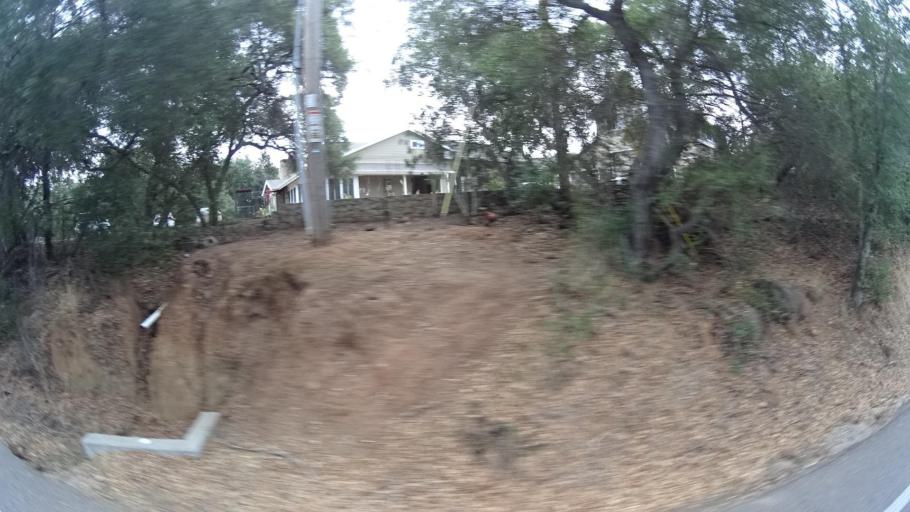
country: US
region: California
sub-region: San Diego County
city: Ramona
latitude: 32.9986
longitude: -116.9299
